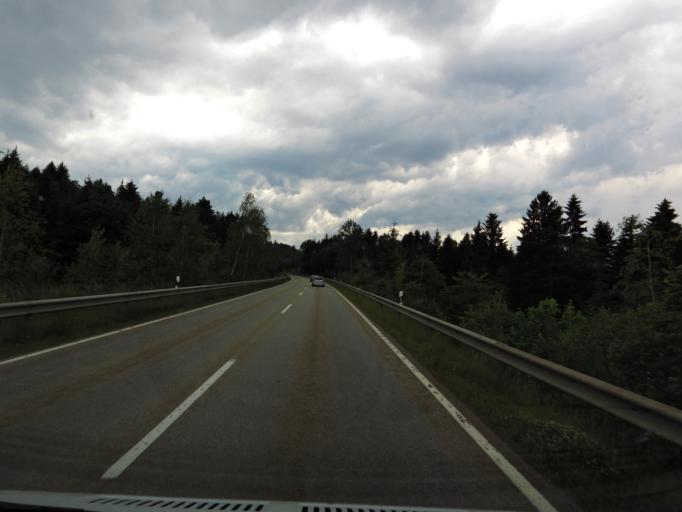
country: DE
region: Bavaria
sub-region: Lower Bavaria
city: Neukirchen vorm Wald
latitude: 48.6931
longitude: 13.4028
